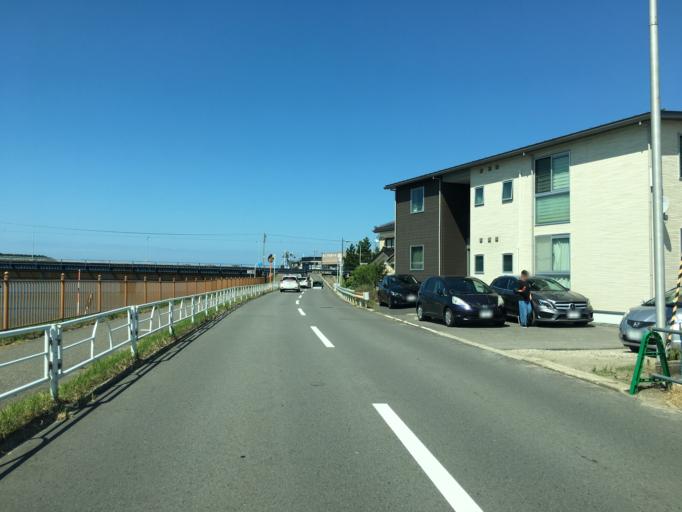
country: JP
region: Niigata
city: Niigata-shi
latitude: 37.9009
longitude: 139.0097
